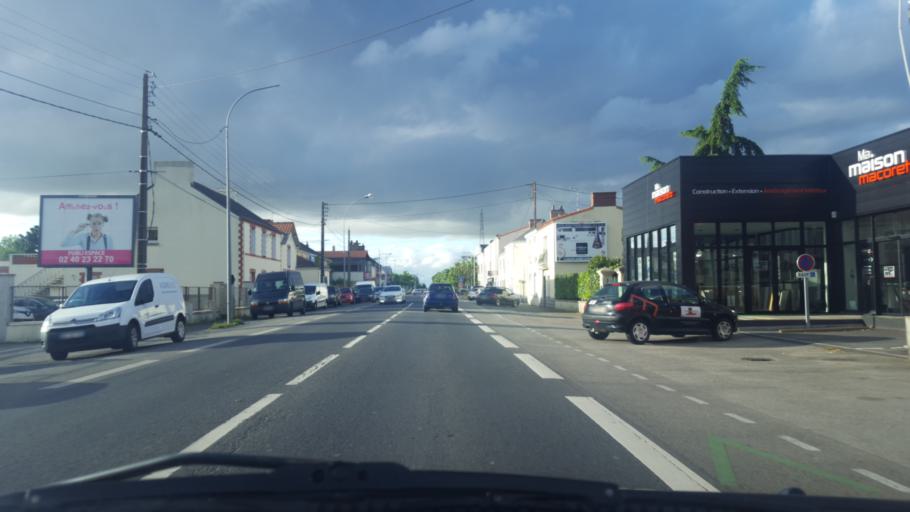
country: FR
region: Pays de la Loire
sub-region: Departement de la Loire-Atlantique
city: Reze
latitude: 47.1634
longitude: -1.5423
